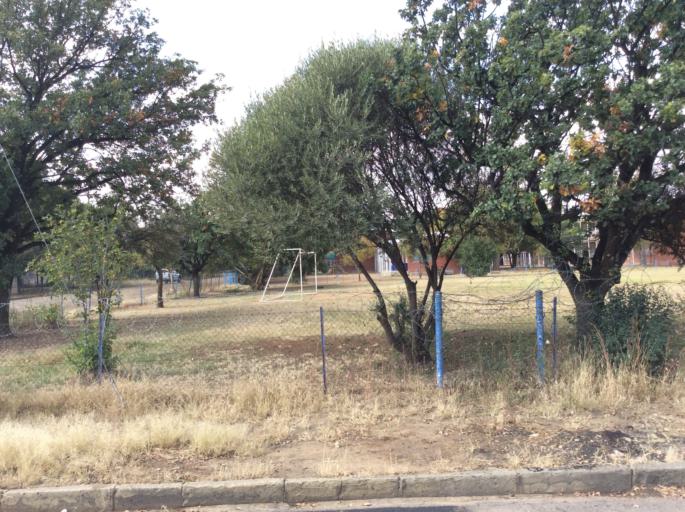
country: LS
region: Mafeteng
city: Mafeteng
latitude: -29.7307
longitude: 27.0387
